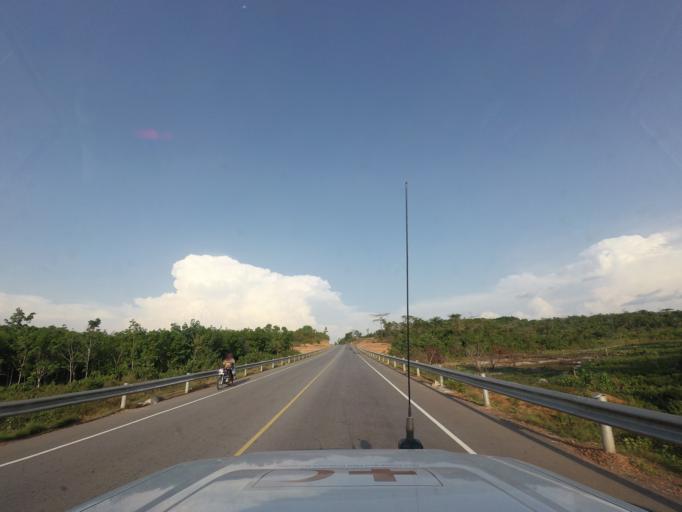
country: LR
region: Bong
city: Gbarnga
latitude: 7.0046
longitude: -9.3121
